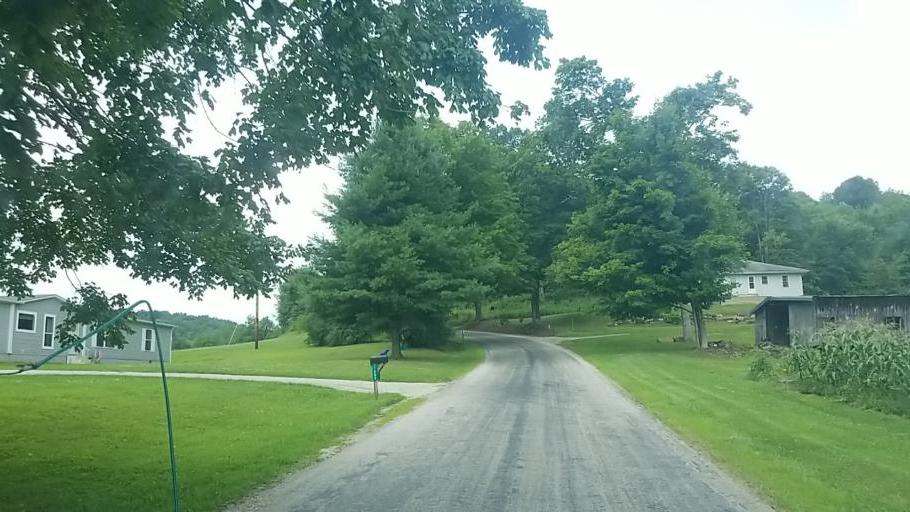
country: US
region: Ohio
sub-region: Muskingum County
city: Frazeysburg
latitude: 40.2225
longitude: -82.2150
